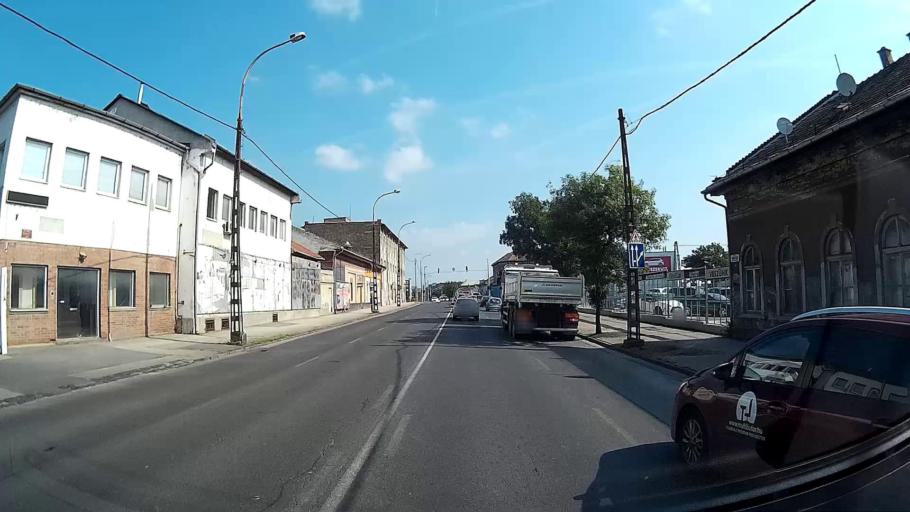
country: HU
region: Budapest
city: Budapest IV. keruelet
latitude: 47.5677
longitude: 19.0800
